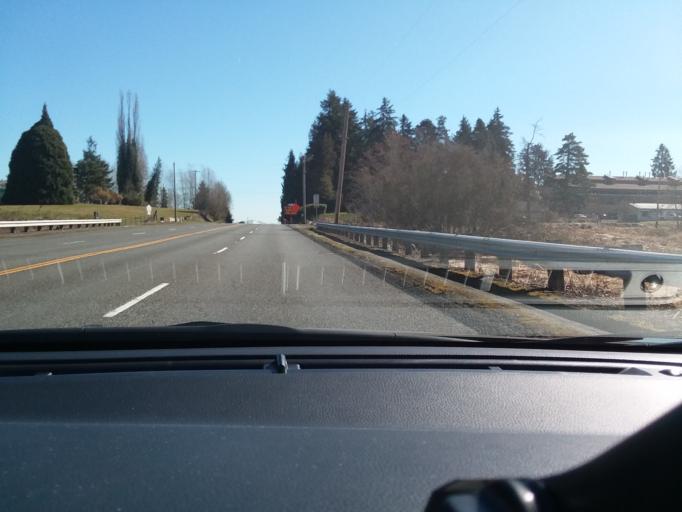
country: US
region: Washington
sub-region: Pierce County
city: Summit
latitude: 47.1902
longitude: -122.3323
